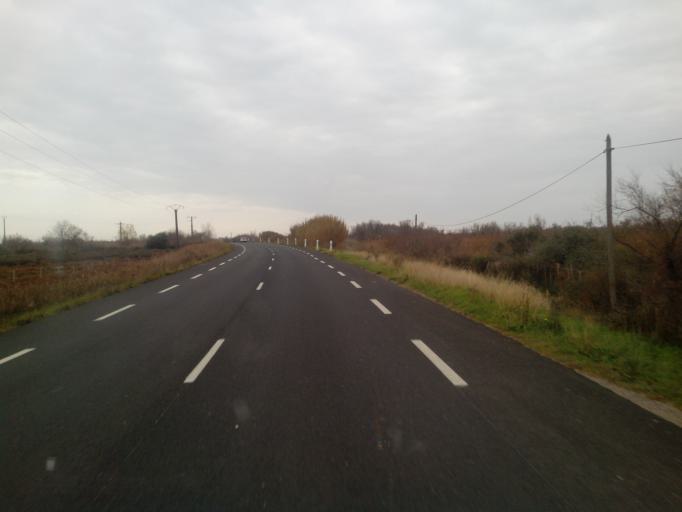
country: FR
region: Languedoc-Roussillon
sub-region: Departement du Gard
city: Aigues-Mortes
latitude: 43.5599
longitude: 4.3174
